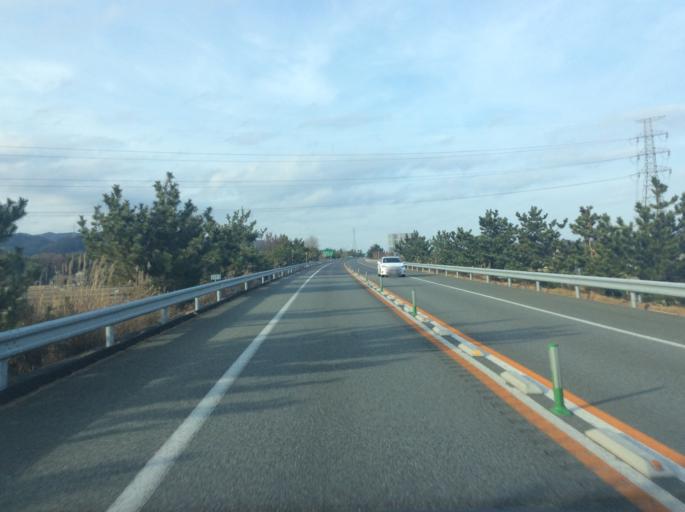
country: JP
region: Fukushima
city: Namie
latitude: 37.3632
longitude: 140.9696
